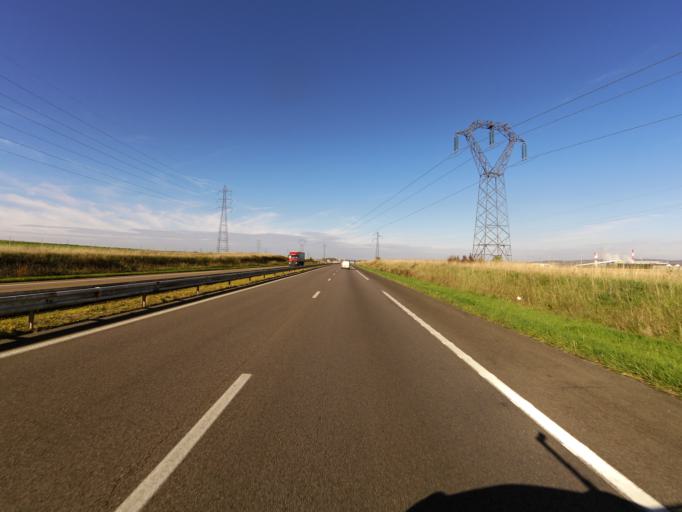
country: FR
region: Champagne-Ardenne
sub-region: Departement de la Marne
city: Verzenay
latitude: 49.1807
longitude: 4.1552
